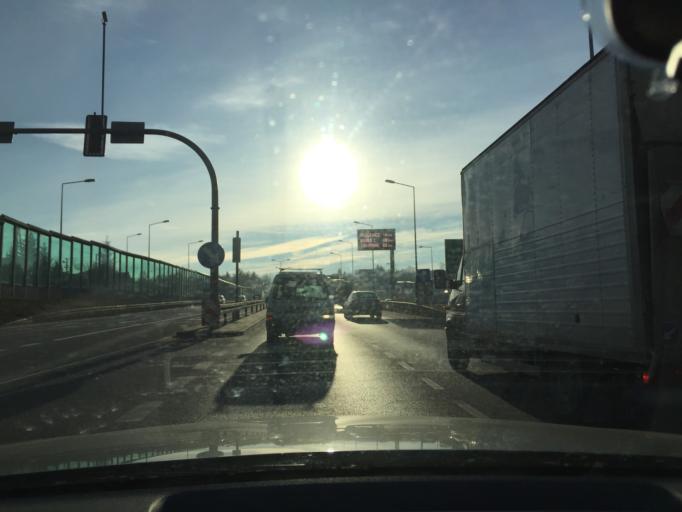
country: PL
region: Lesser Poland Voivodeship
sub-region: Powiat krakowski
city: Libertow
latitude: 49.9789
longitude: 19.9101
